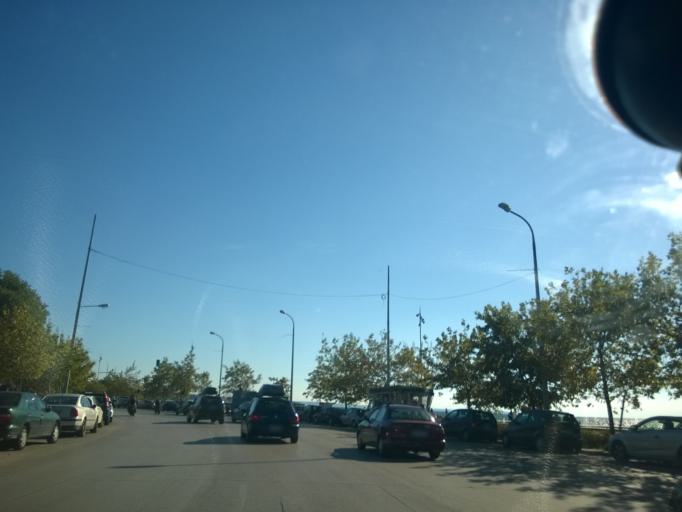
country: GR
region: Central Macedonia
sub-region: Nomos Thessalonikis
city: Agios Pavlos
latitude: 40.6225
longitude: 22.9519
